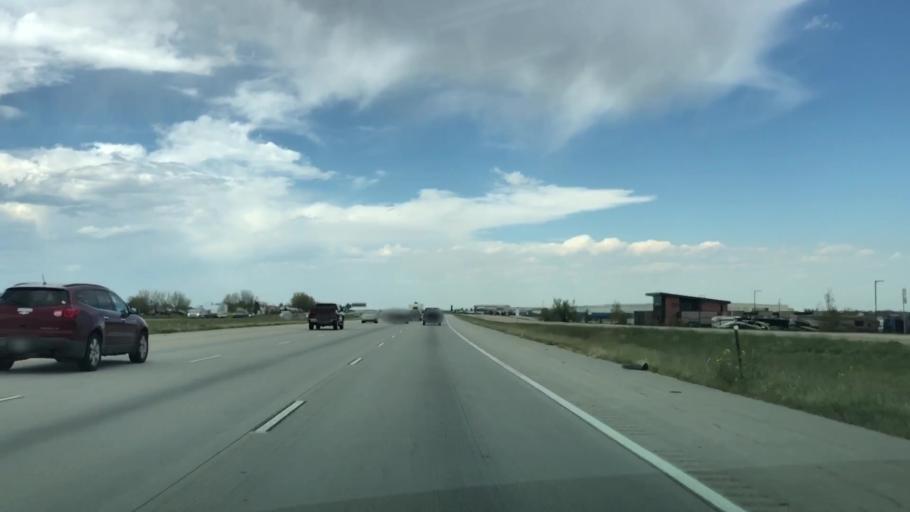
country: US
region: Colorado
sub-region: Weld County
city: Firestone
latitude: 40.1121
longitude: -104.9800
